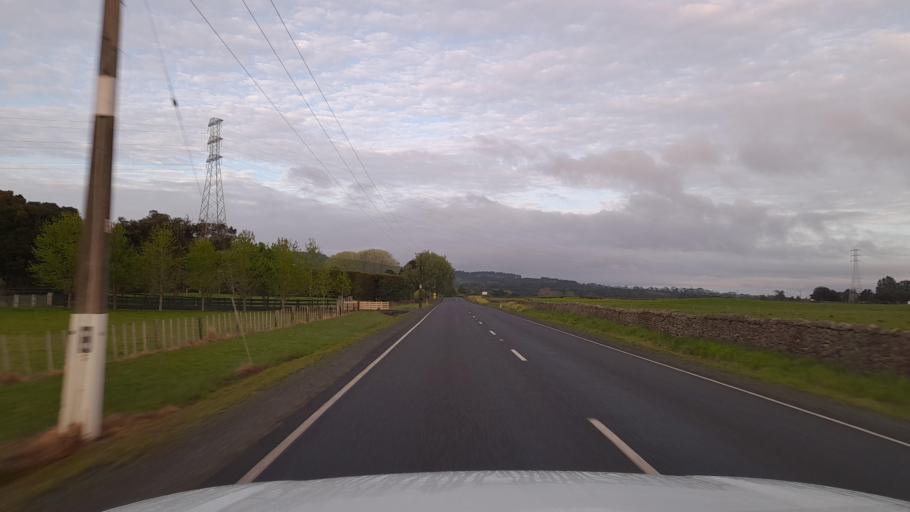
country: NZ
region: Northland
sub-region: Whangarei
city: Maungatapere
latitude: -35.7546
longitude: 174.1879
